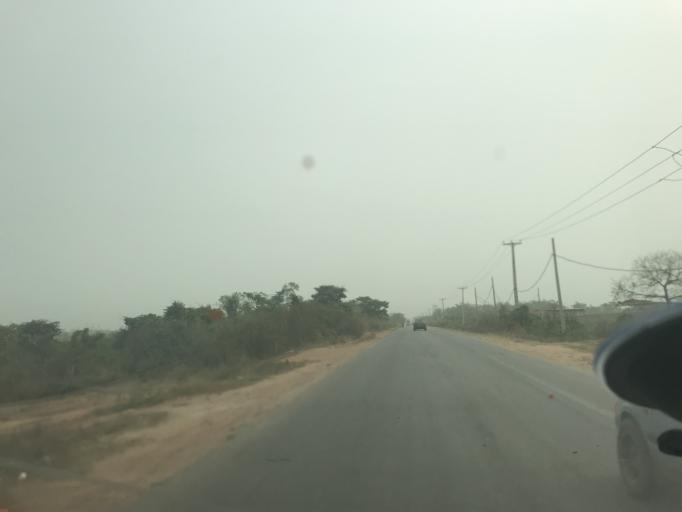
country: NG
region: Ogun
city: Itori
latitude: 6.8908
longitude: 3.1726
